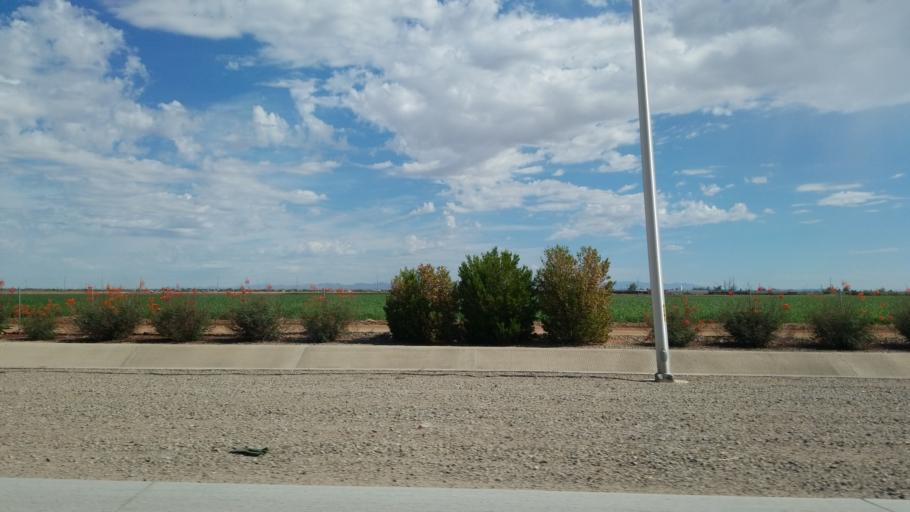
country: US
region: Arizona
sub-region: Maricopa County
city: Citrus Park
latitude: 33.5592
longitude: -112.3800
